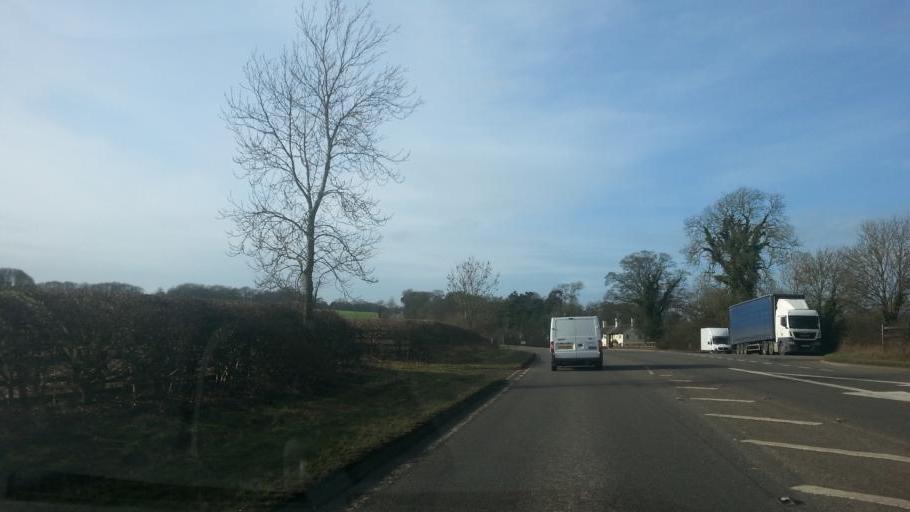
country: GB
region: England
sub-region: District of Rutland
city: Ridlington
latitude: 52.5957
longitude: -0.8499
